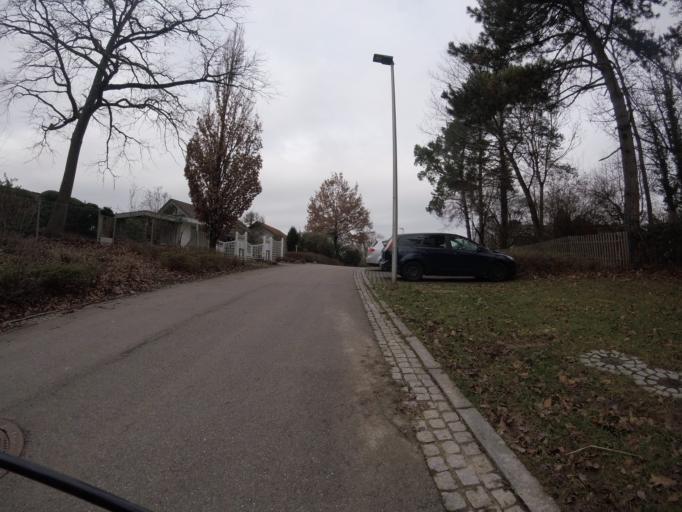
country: DE
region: Baden-Wuerttemberg
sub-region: Regierungsbezirk Stuttgart
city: Backnang
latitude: 48.9403
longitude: 9.4223
